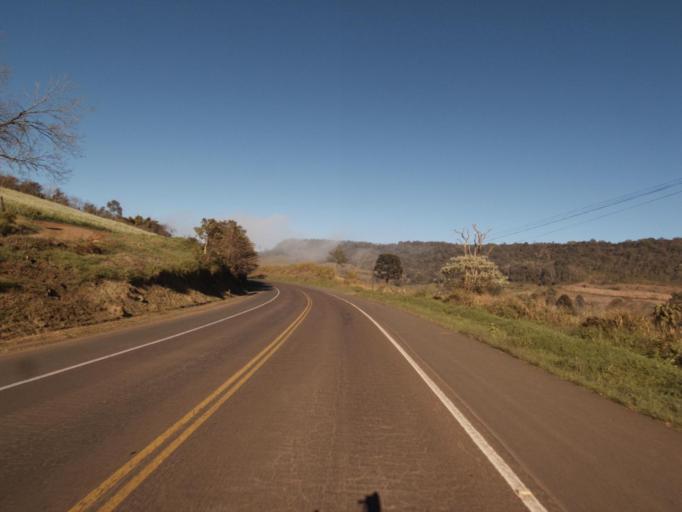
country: BR
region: Rio Grande do Sul
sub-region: Frederico Westphalen
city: Frederico Westphalen
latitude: -26.9676
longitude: -53.2159
